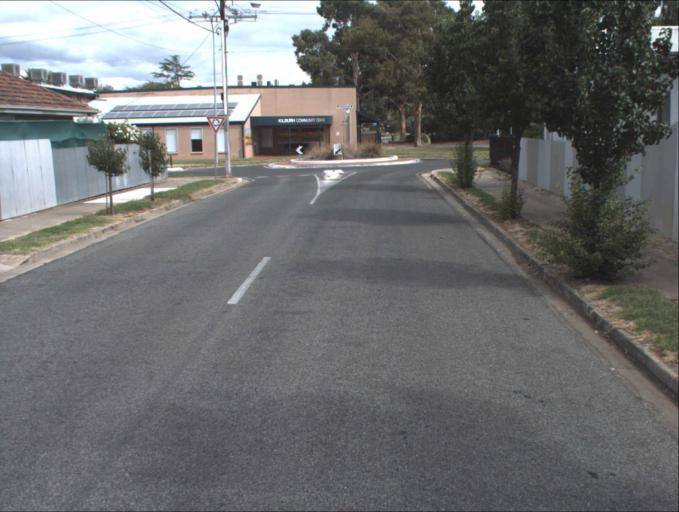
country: AU
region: South Australia
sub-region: Port Adelaide Enfield
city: Blair Athol
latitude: -34.8628
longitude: 138.5895
